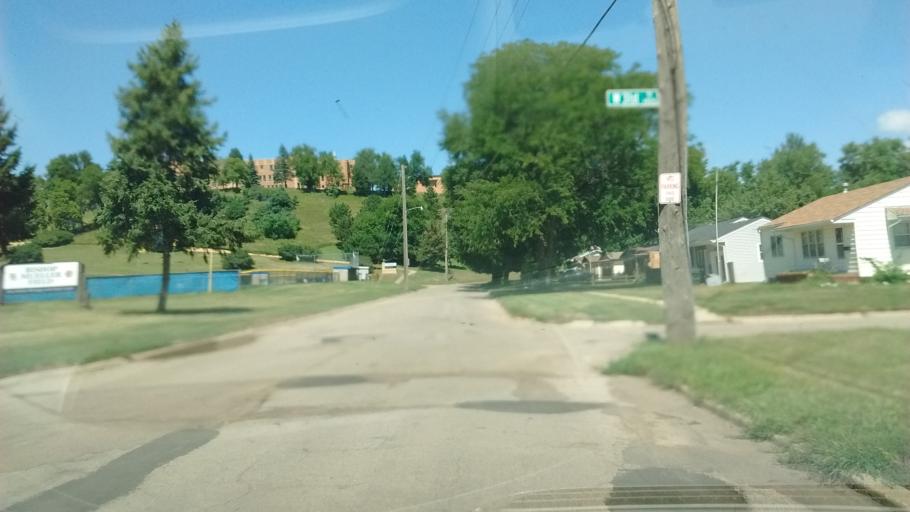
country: US
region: Iowa
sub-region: Woodbury County
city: Sioux City
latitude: 42.5239
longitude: -96.4256
